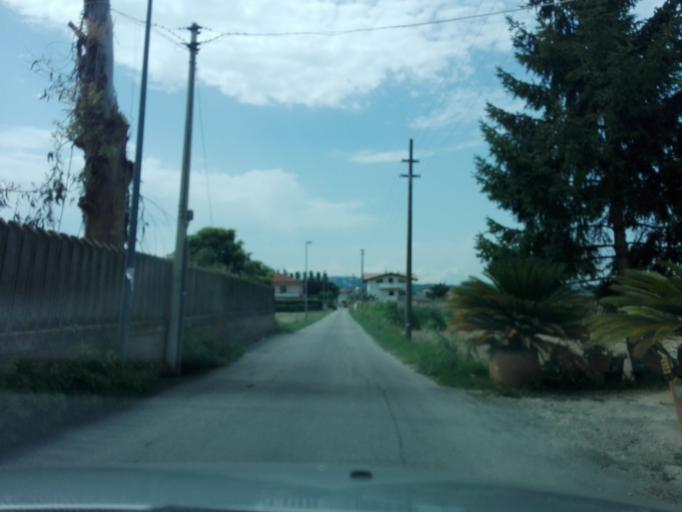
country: IT
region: Abruzzo
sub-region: Provincia di Pescara
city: Cappelle sul Tavo
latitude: 42.4895
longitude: 14.1208
